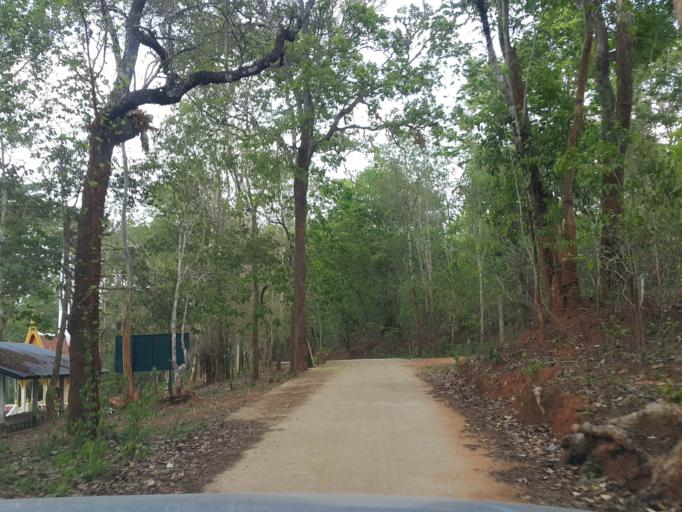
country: TH
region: Chiang Mai
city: Wiang Haeng
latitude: 19.3703
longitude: 98.7189
